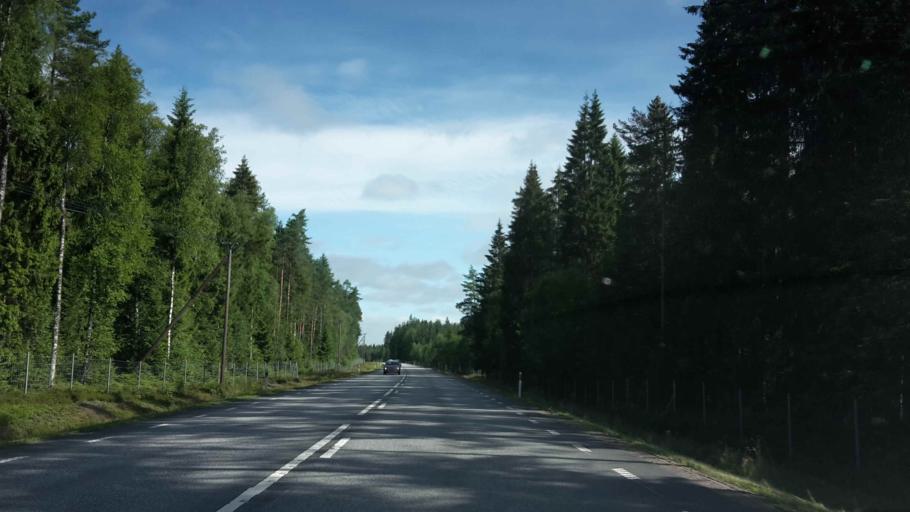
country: SE
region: OErebro
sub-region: Askersunds Kommun
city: Asbro
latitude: 58.9504
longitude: 15.0323
